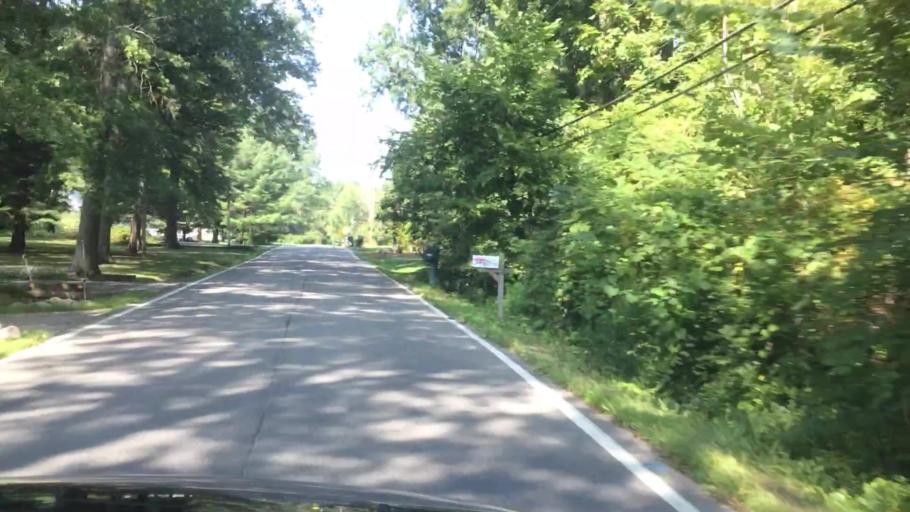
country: US
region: Ohio
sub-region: Summit County
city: Silver Lake
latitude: 41.1885
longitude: -81.4579
